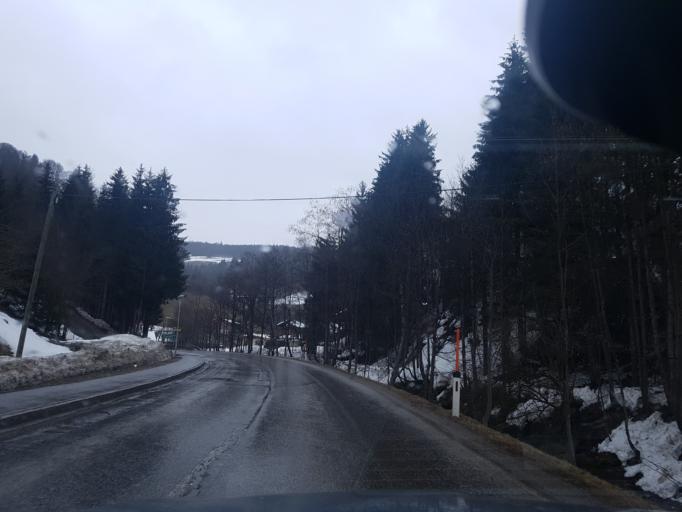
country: AT
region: Tyrol
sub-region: Politischer Bezirk Kufstein
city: Worgl
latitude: 47.4538
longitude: 12.0898
